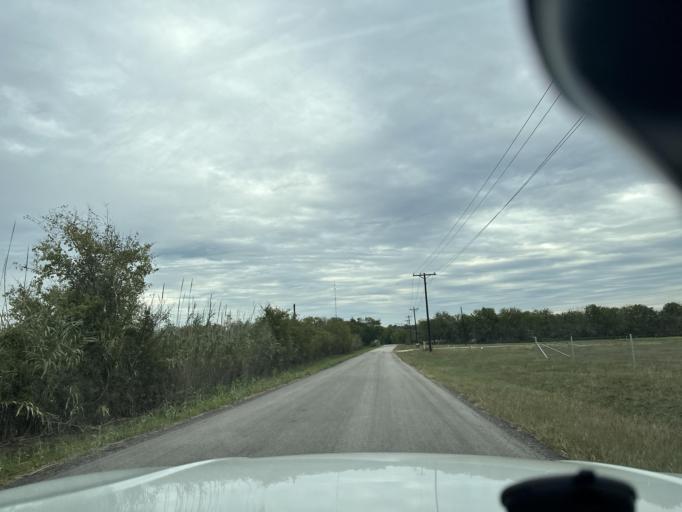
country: US
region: Texas
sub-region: Burleson County
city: Somerville
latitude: 30.1617
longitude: -96.6452
